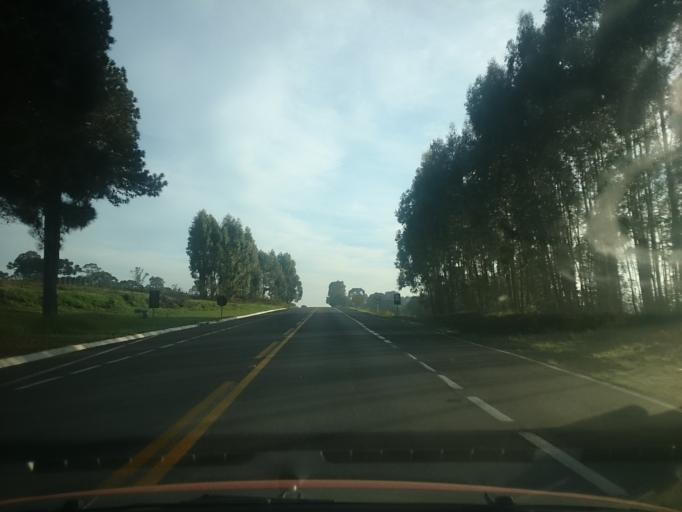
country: BR
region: Rio Grande do Sul
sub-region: Vacaria
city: Vacaria
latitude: -28.2856
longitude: -50.8026
